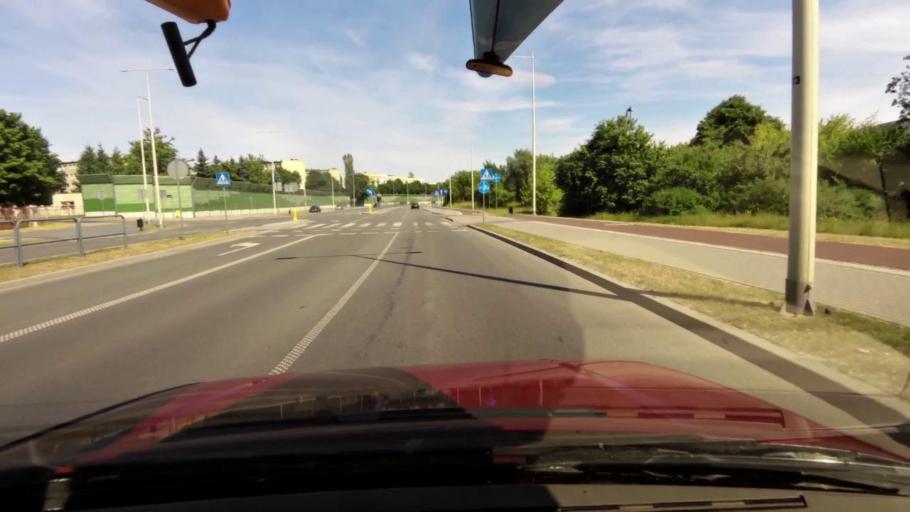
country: PL
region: Pomeranian Voivodeship
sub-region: Powiat slupski
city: Kobylnica
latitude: 54.4566
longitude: 16.9959
